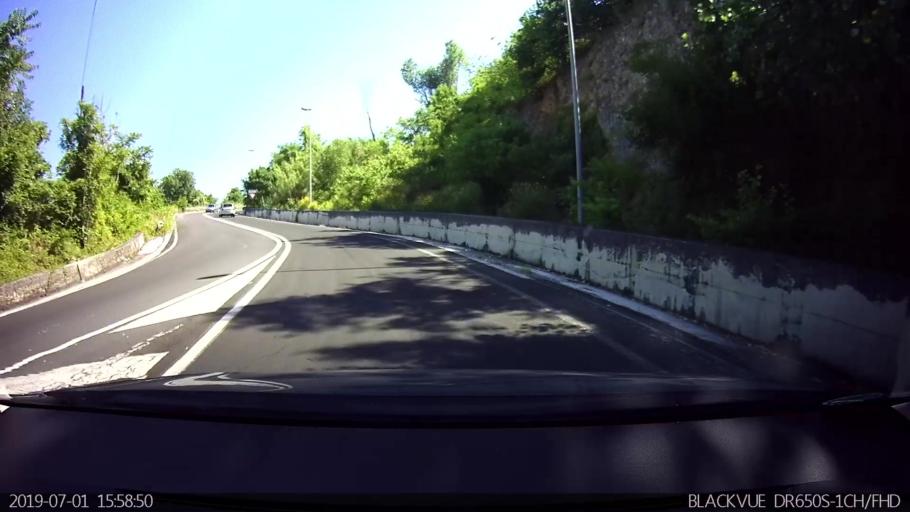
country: IT
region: Latium
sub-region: Provincia di Frosinone
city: Sant'Angelo in Villa-Giglio
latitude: 41.6651
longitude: 13.4243
